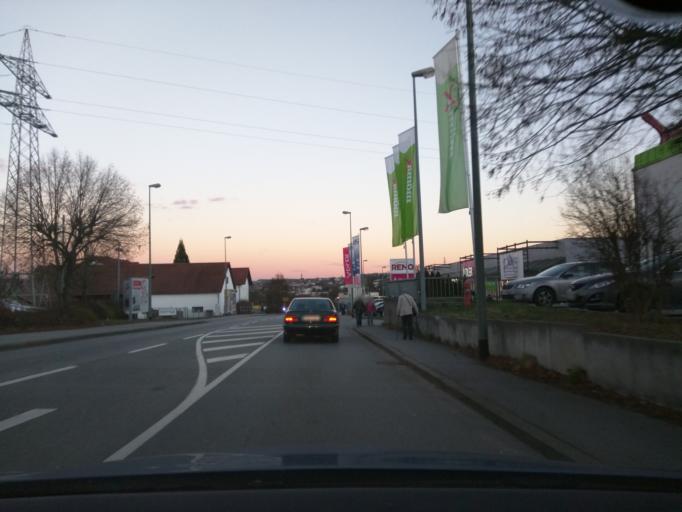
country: DE
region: Bavaria
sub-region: Lower Bavaria
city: Passau
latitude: 48.5739
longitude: 13.4078
